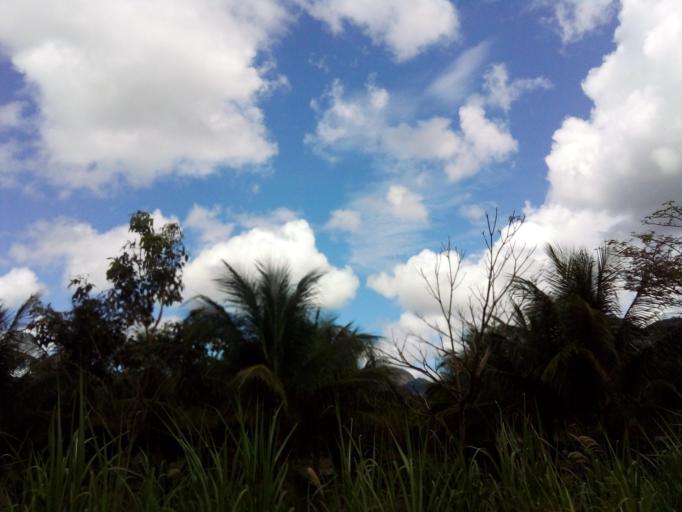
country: BR
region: Espirito Santo
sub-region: Ibiracu
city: Ibiracu
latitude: -19.8788
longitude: -40.3623
